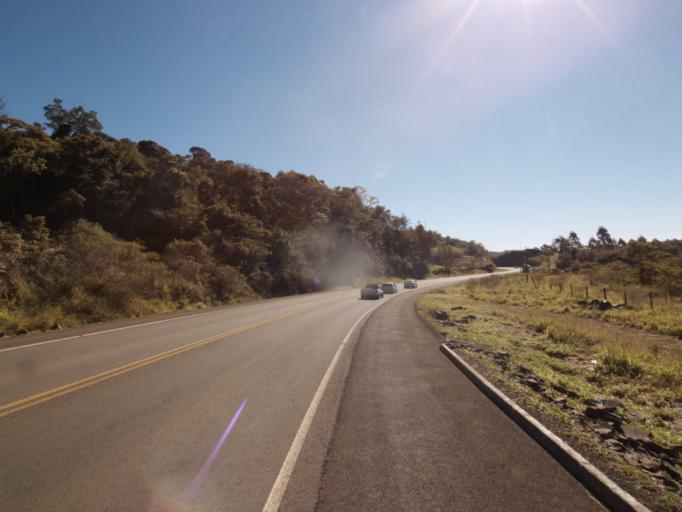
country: AR
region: Misiones
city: Bernardo de Irigoyen
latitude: -26.6997
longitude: -53.5331
